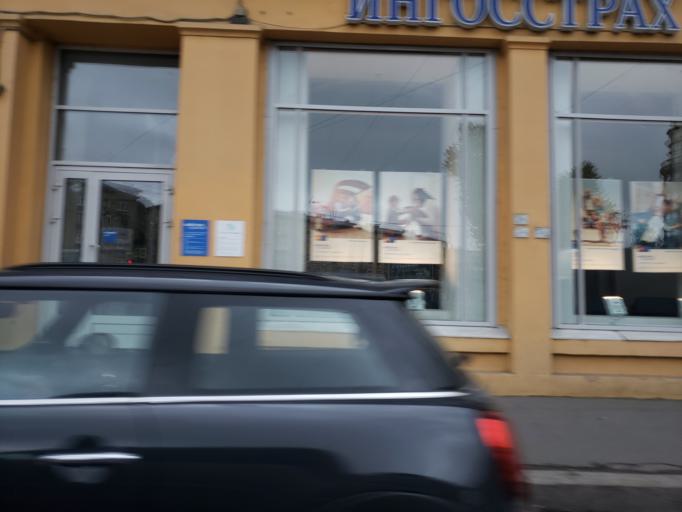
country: RU
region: St.-Petersburg
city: Vasyl'evsky Ostrov
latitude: 59.9380
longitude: 30.2323
